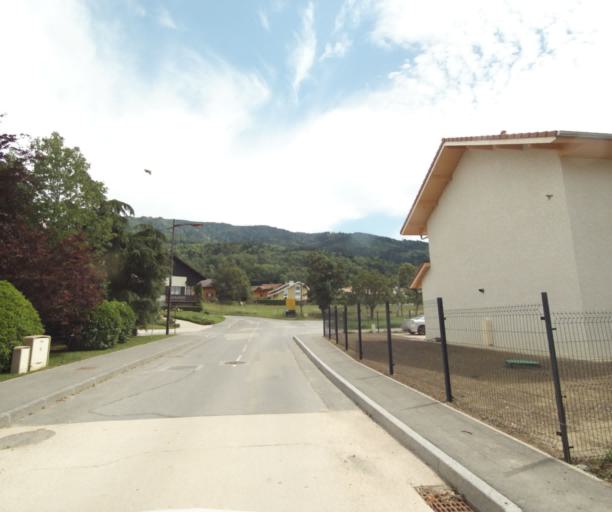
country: FR
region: Rhone-Alpes
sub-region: Departement de la Haute-Savoie
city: Bons-en-Chablais
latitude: 46.2740
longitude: 6.4120
